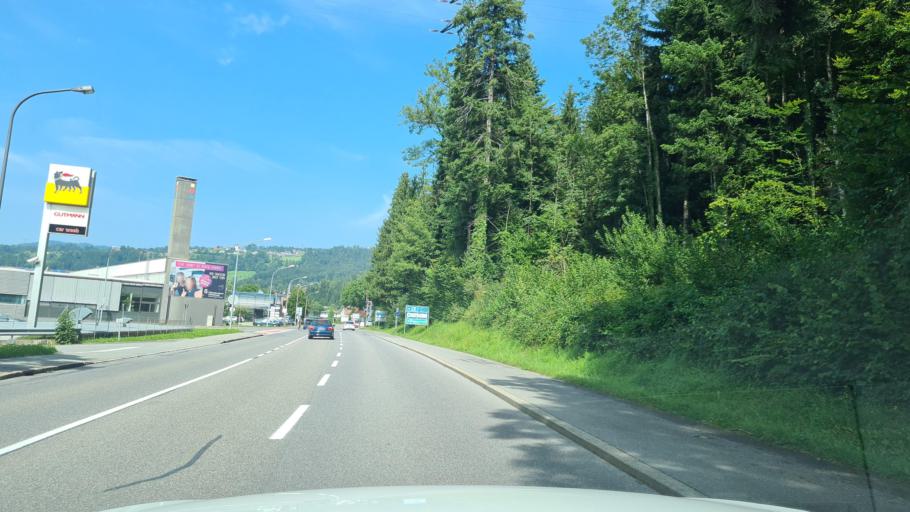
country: AT
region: Vorarlberg
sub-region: Politischer Bezirk Bregenz
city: Schwarzach
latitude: 47.4381
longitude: 9.7594
